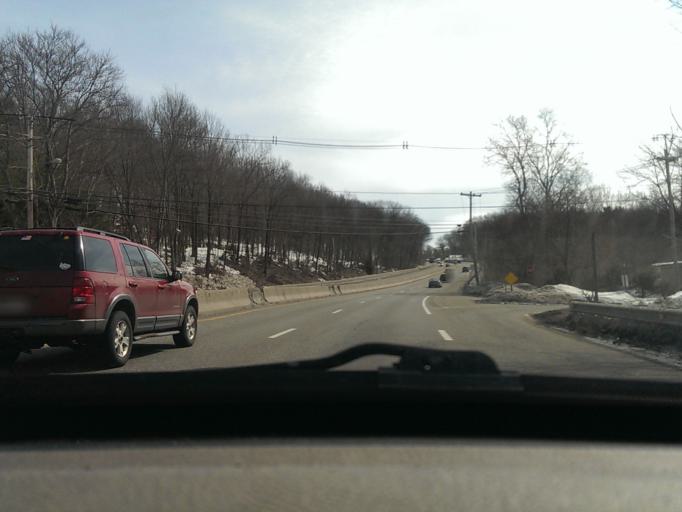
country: US
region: Massachusetts
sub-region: Worcester County
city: Millbury
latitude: 42.1848
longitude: -71.7635
